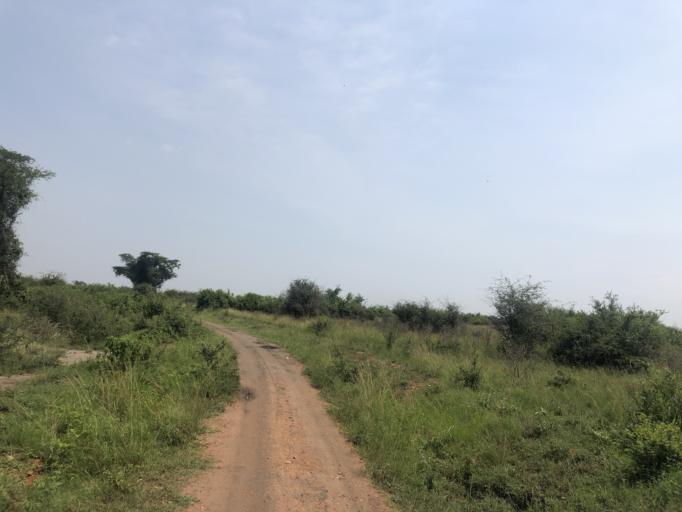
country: UG
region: Western Region
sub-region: Rubirizi District
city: Rubirizi
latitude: -0.2125
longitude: 29.9540
